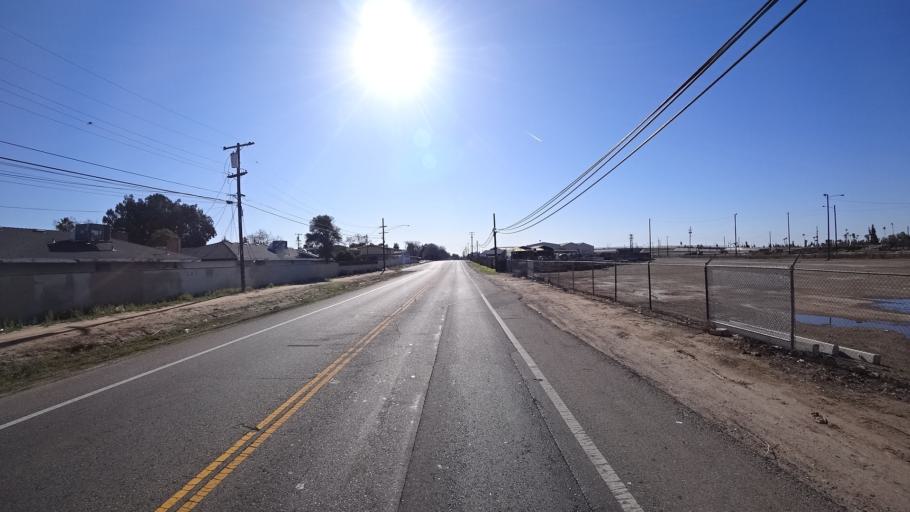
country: US
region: California
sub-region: Fresno County
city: West Park
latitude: 36.7770
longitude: -119.8393
